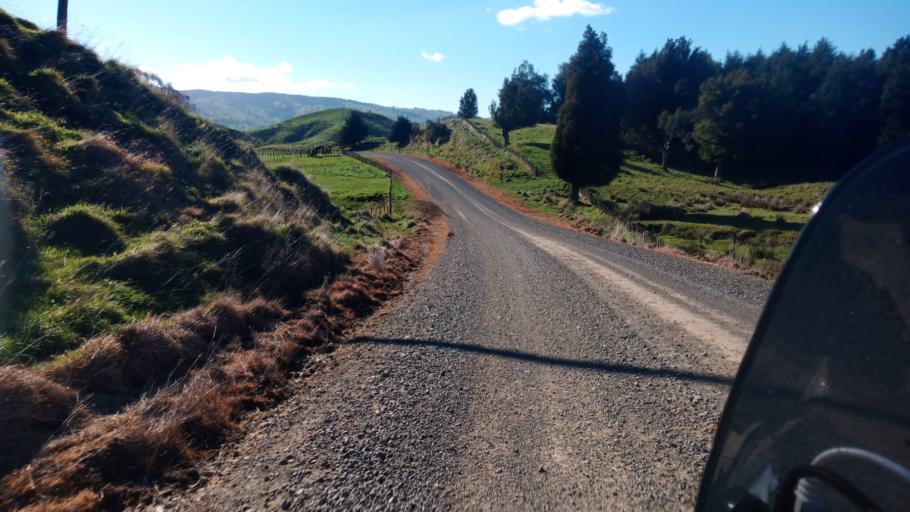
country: NZ
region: Hawke's Bay
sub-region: Wairoa District
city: Wairoa
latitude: -38.7635
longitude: 177.2635
